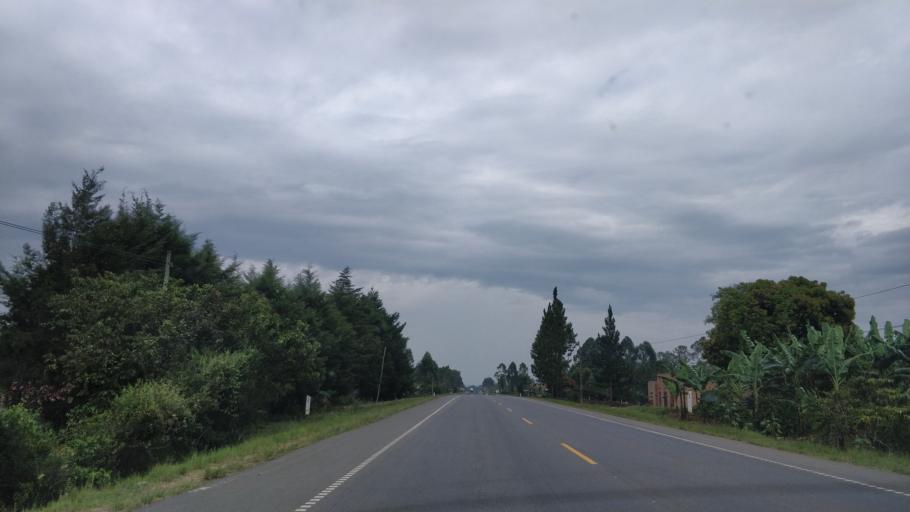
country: UG
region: Western Region
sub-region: Sheema District
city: Kibingo
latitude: -0.6729
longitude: 30.4279
